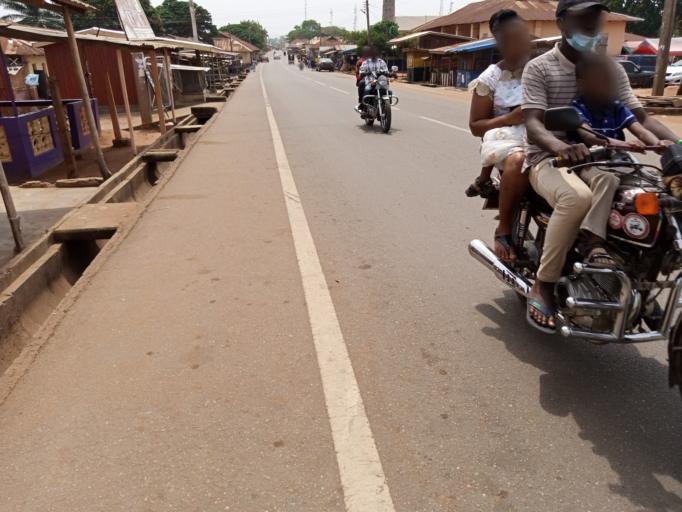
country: GH
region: Volta
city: Kpandu
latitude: 7.0003
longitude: 0.2946
